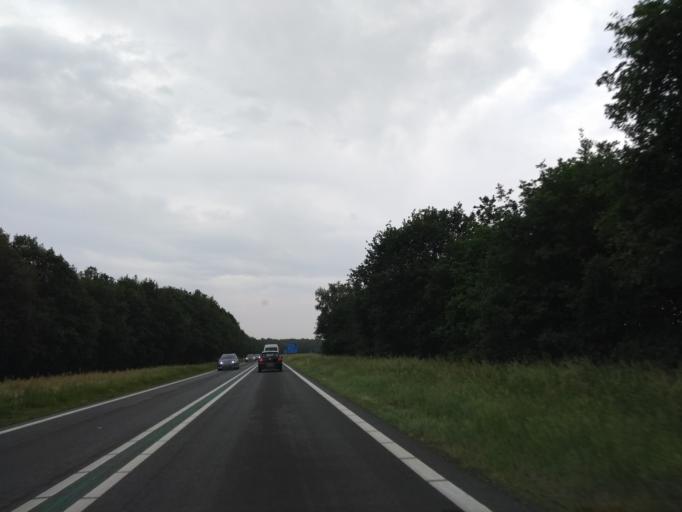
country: NL
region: Overijssel
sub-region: Gemeente Twenterand
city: Westerhaar-Vriezenveensewijk
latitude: 52.4764
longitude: 6.6171
